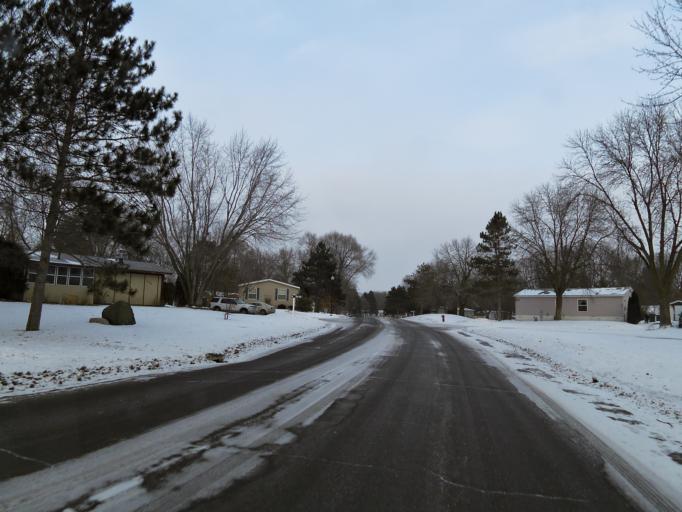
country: US
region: Minnesota
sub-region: Washington County
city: Lake Elmo
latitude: 44.9616
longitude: -92.8785
